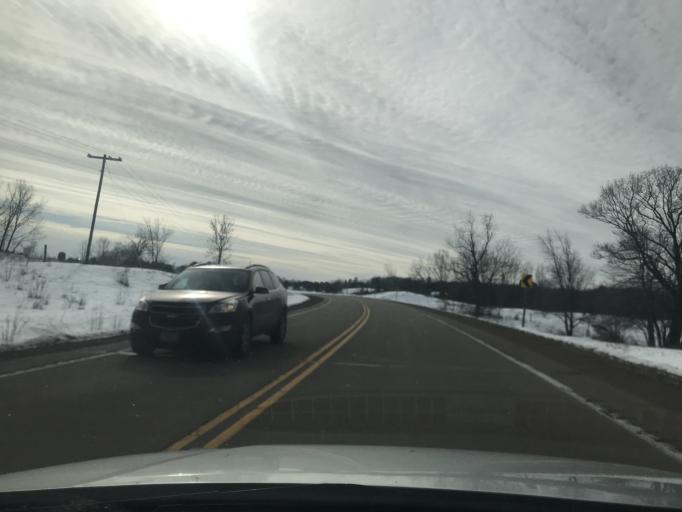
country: US
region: Wisconsin
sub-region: Oconto County
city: Gillett
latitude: 44.8788
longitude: -88.3483
